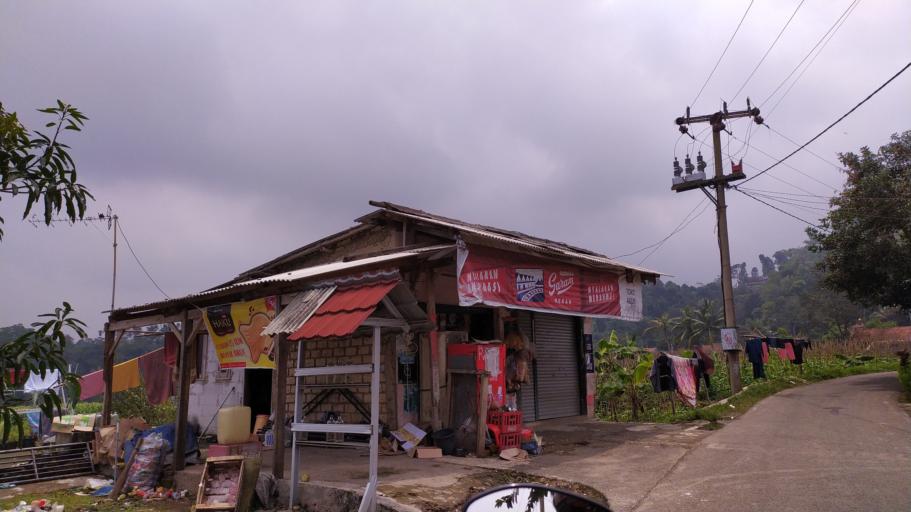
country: ID
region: West Java
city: Ciampea
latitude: -6.6235
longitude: 106.7122
